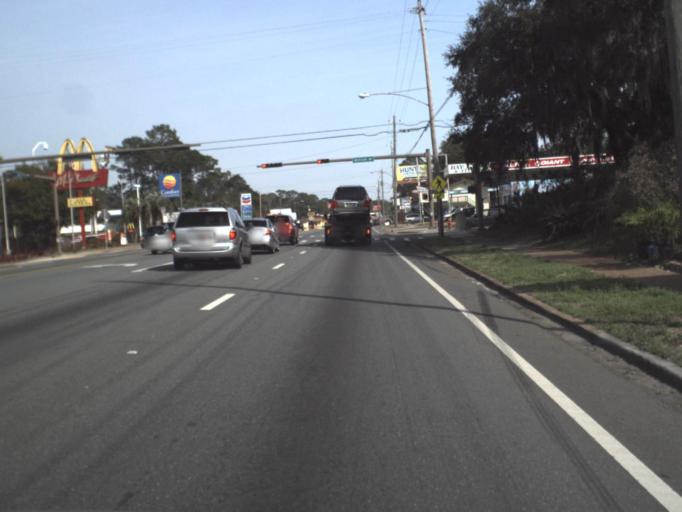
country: US
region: Florida
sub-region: Bay County
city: Pretty Bayou
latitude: 30.1807
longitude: -85.7094
